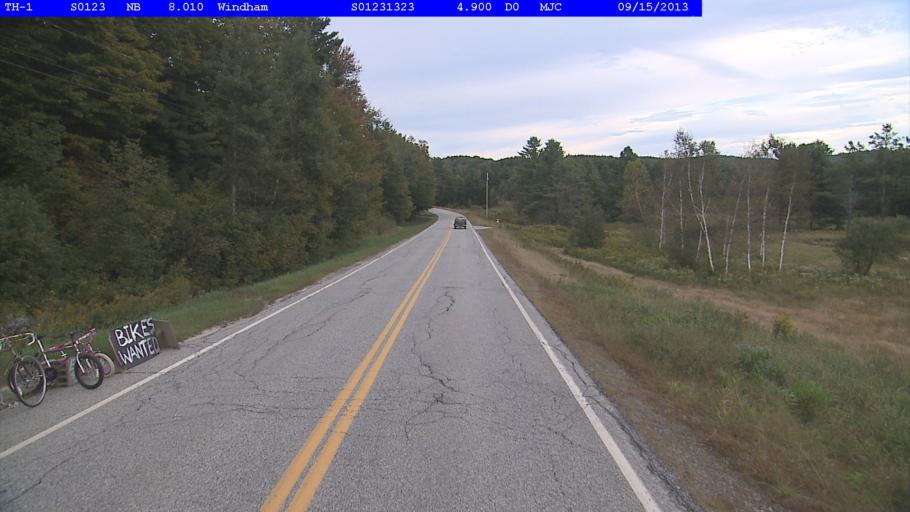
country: US
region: Vermont
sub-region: Windsor County
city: Chester
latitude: 43.1936
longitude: -72.7214
